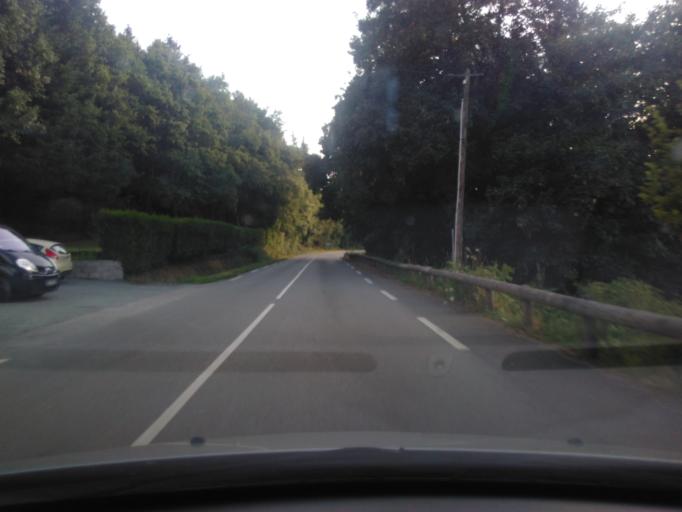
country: FR
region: Pays de la Loire
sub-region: Departement de la Vendee
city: Nesmy
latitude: 46.5827
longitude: -1.3599
